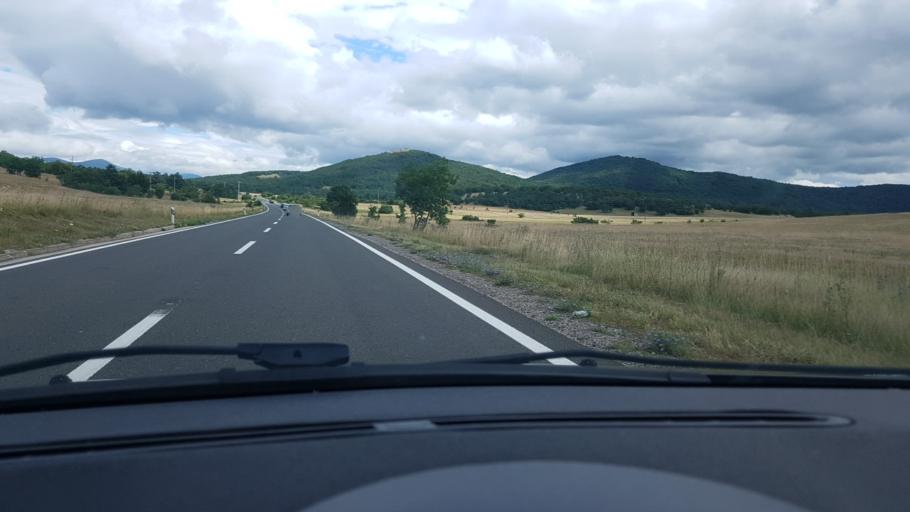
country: HR
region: Zadarska
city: Gracac
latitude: 44.4670
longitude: 15.7994
